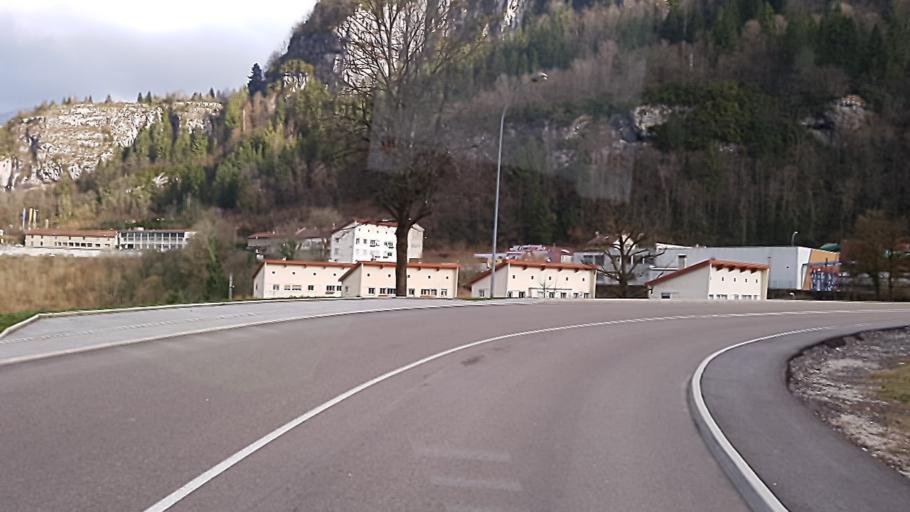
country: FR
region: Franche-Comte
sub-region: Departement du Jura
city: Saint-Claude
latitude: 46.3822
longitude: 5.8561
